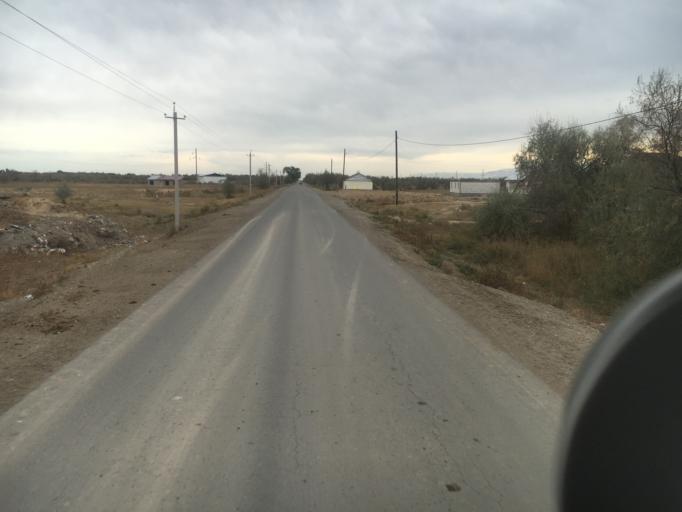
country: KZ
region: Almaty Oblysy
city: Energeticheskiy
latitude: 43.5860
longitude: 77.0658
